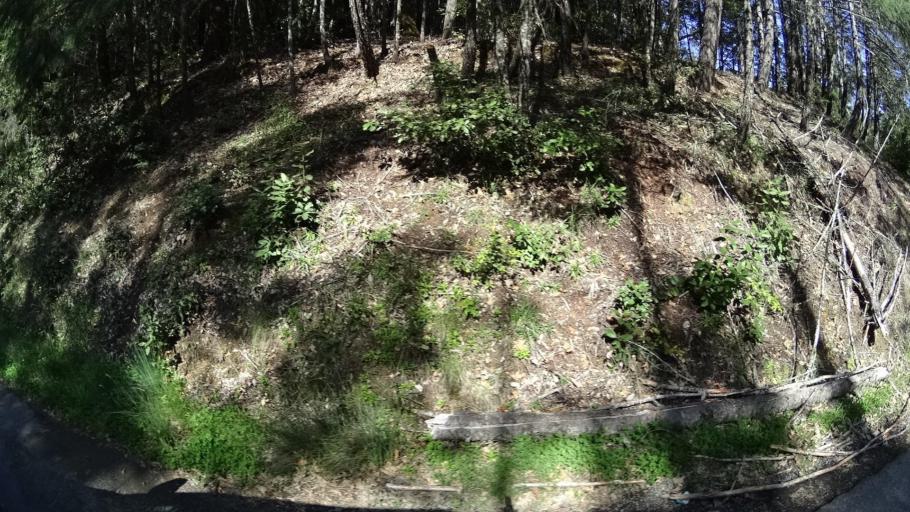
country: US
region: California
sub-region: Humboldt County
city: Redway
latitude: 40.0757
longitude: -123.6521
